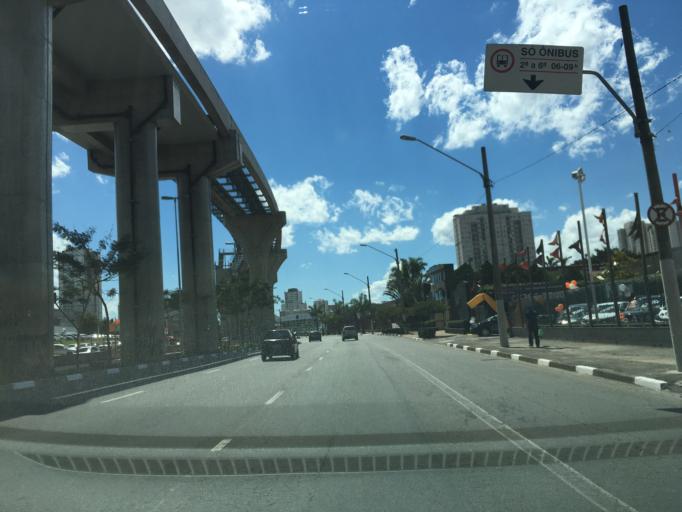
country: BR
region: Sao Paulo
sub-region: Sao Caetano Do Sul
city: Sao Caetano do Sul
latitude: -23.5818
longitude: -46.5581
